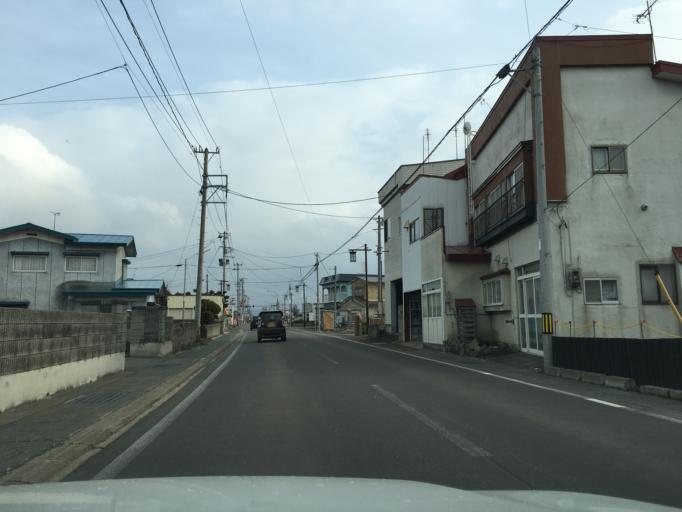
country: JP
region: Aomori
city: Namioka
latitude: 40.7102
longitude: 140.5898
